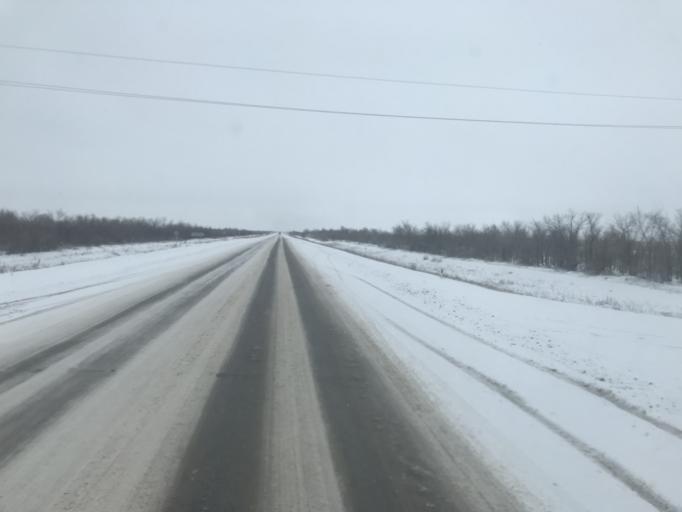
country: KZ
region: Batys Qazaqstan
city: Oral
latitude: 51.0499
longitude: 51.5709
